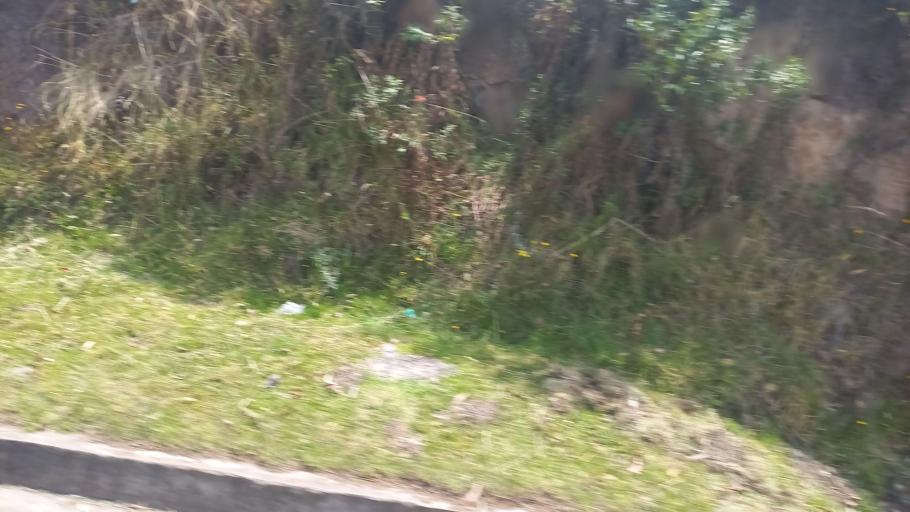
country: EC
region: Pichincha
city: Cayambe
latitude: 0.1780
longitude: -78.0917
